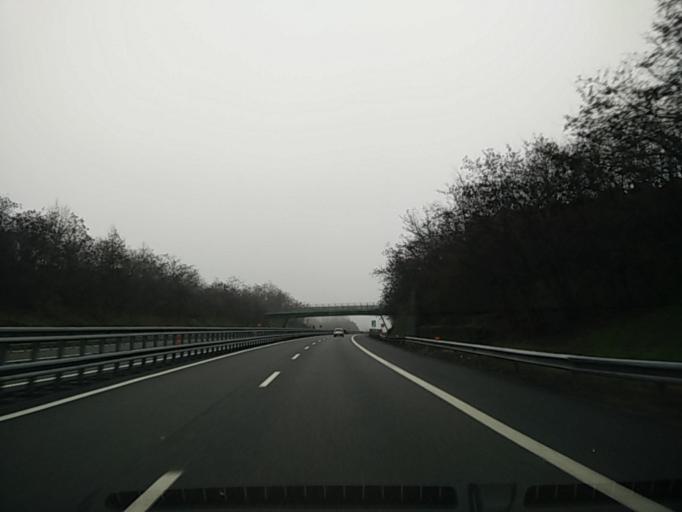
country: IT
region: Piedmont
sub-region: Provincia di Asti
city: Castello di Annone
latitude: 44.9107
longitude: 8.2943
